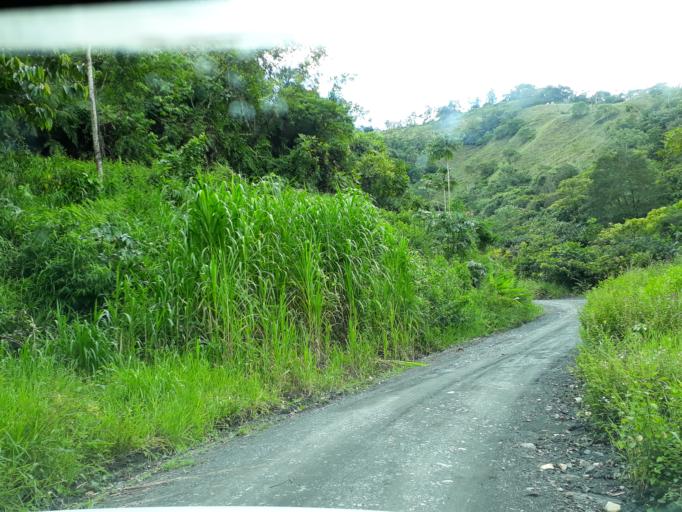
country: CO
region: Boyaca
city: Quipama
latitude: 5.4595
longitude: -74.1768
